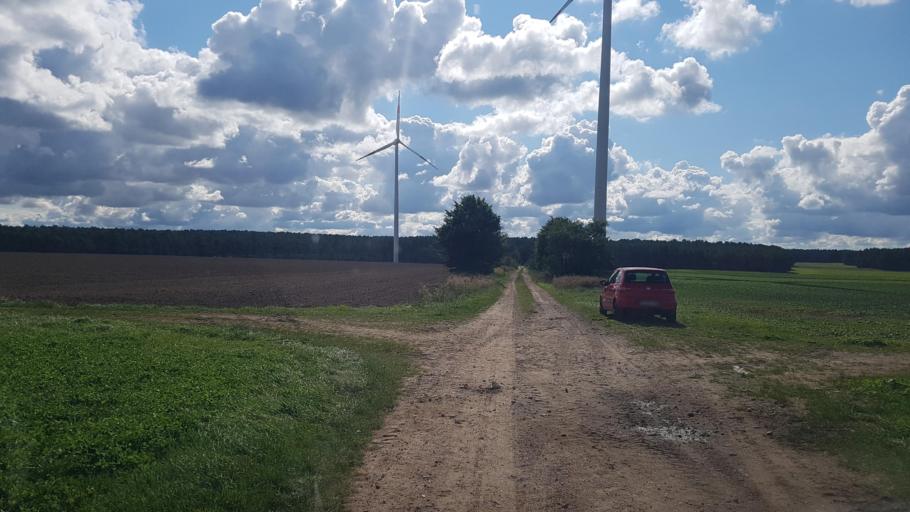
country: DE
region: Brandenburg
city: Niemegk
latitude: 52.0796
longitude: 12.7303
